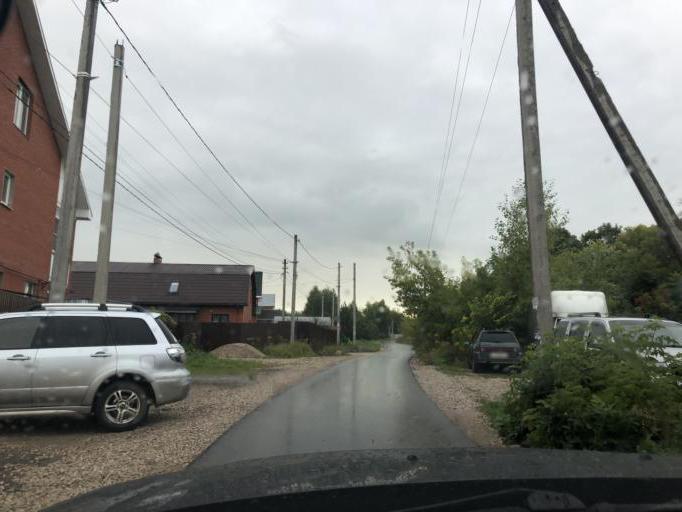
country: RU
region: Tula
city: Barsuki
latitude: 54.2023
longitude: 37.5264
